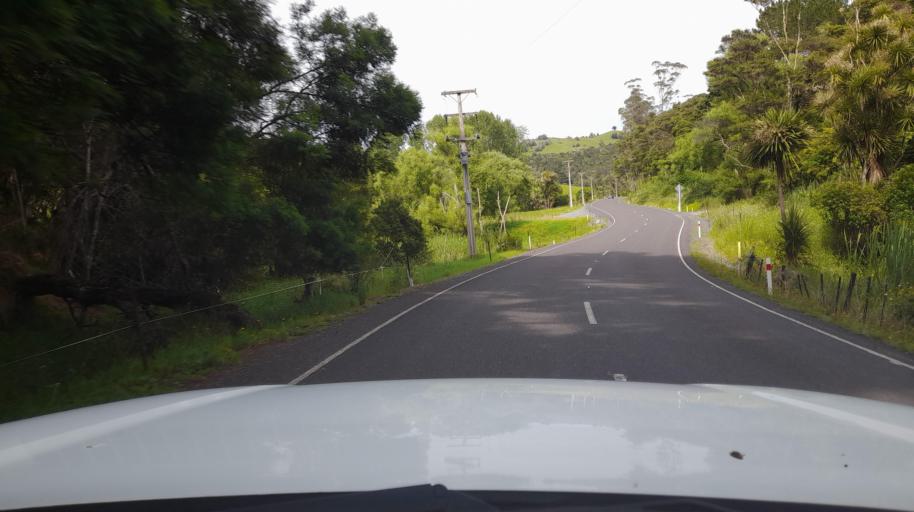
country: NZ
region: Northland
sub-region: Far North District
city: Taipa
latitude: -35.2400
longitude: 173.5414
